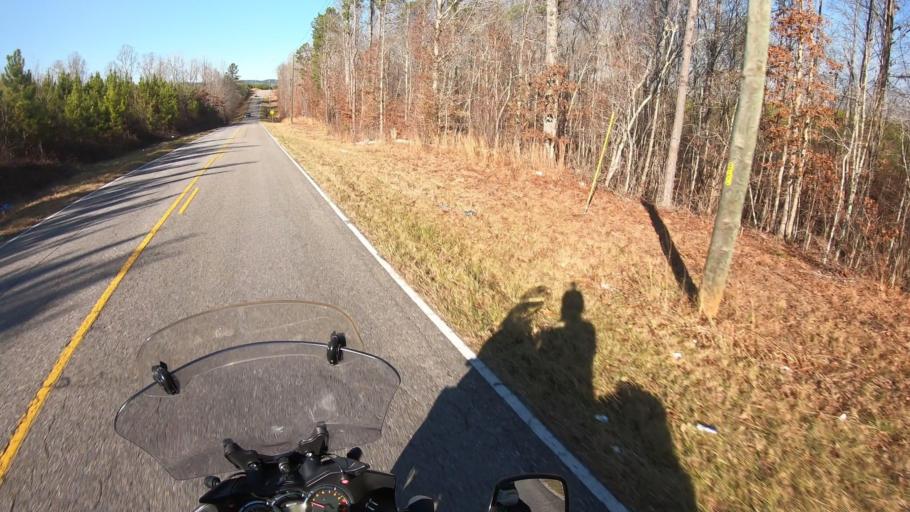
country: US
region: Alabama
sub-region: Cleburne County
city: Heflin
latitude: 33.7369
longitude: -85.4769
